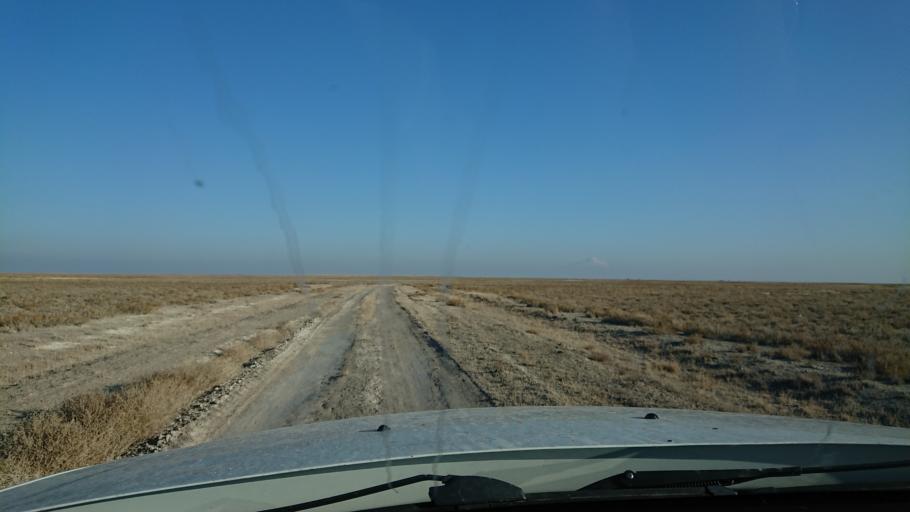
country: TR
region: Aksaray
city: Eskil
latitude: 38.4074
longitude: 33.5680
